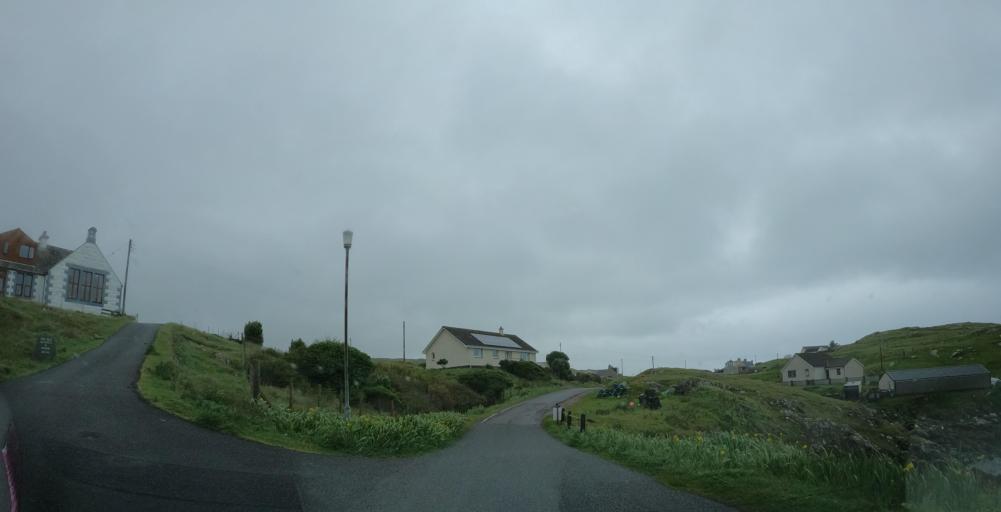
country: GB
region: Scotland
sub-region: Eilean Siar
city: Barra
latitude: 56.9641
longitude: -7.4381
